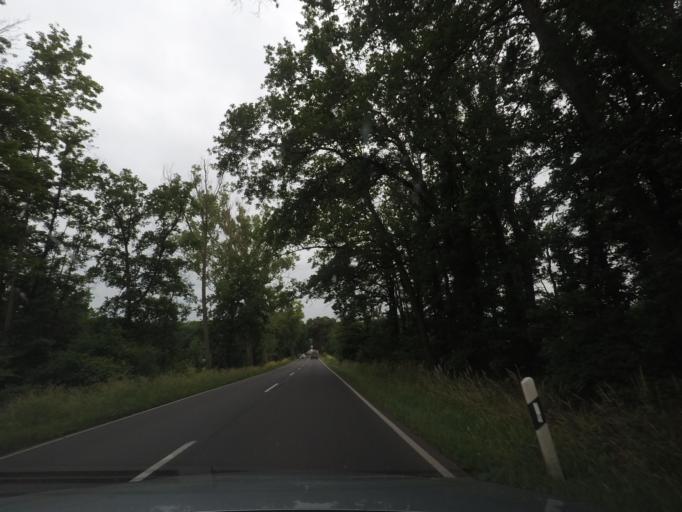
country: DE
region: Saxony-Anhalt
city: Haldensleben I
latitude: 52.2706
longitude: 11.3771
